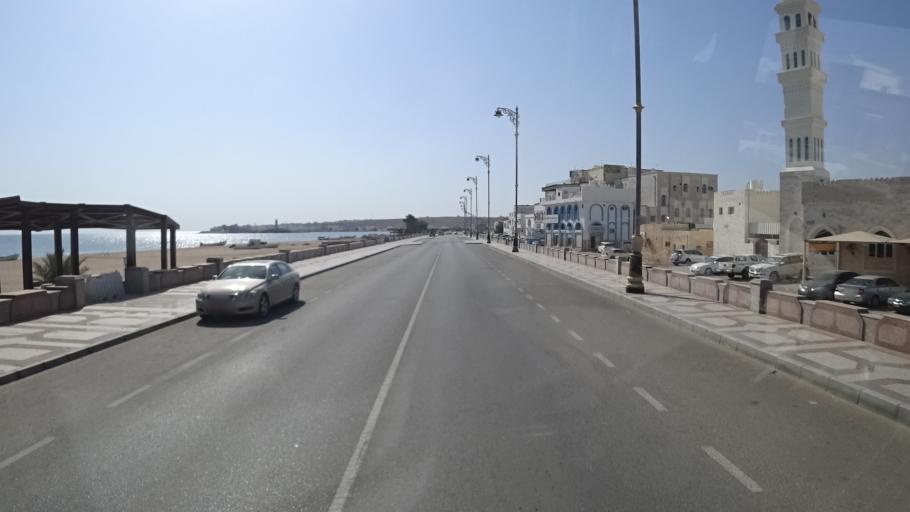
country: OM
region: Ash Sharqiyah
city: Sur
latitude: 22.5710
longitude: 59.5299
